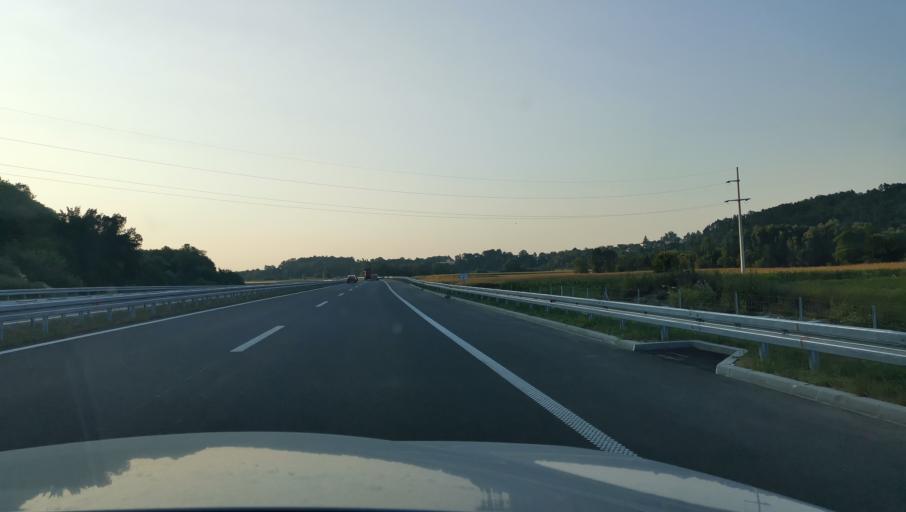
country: RS
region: Central Serbia
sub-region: Kolubarski Okrug
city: Lajkovac
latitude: 44.3385
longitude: 20.1984
